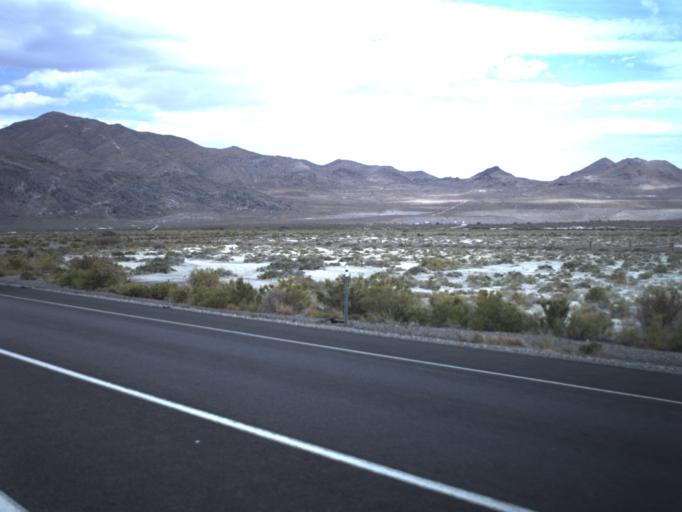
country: US
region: Utah
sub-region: Tooele County
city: Wendover
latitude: 40.7461
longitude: -113.9950
